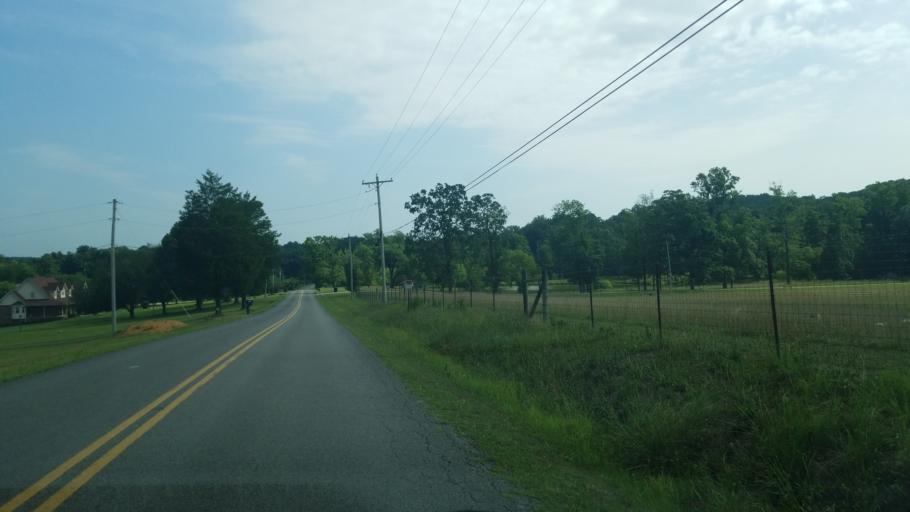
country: US
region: Tennessee
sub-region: Hamilton County
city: Apison
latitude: 35.0368
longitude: -84.9934
